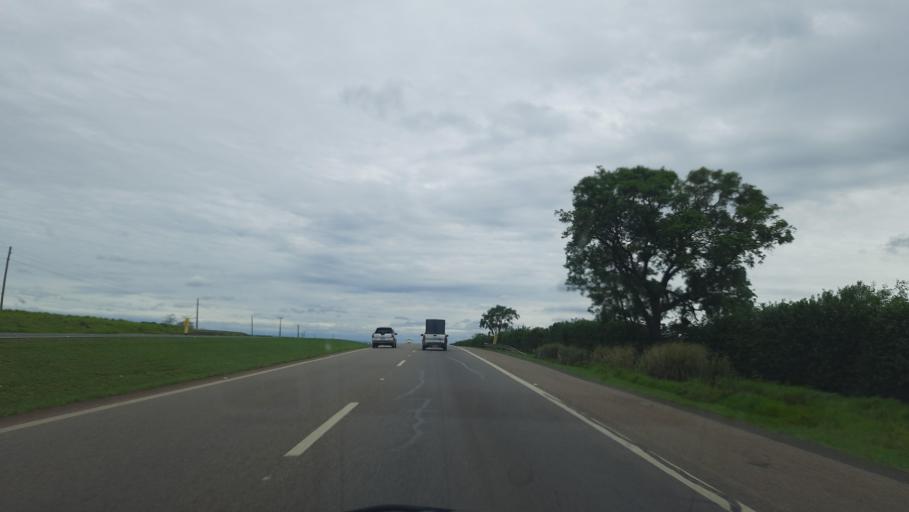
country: BR
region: Sao Paulo
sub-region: Moji-Guacu
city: Mogi-Gaucu
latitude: -22.2547
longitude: -46.9775
